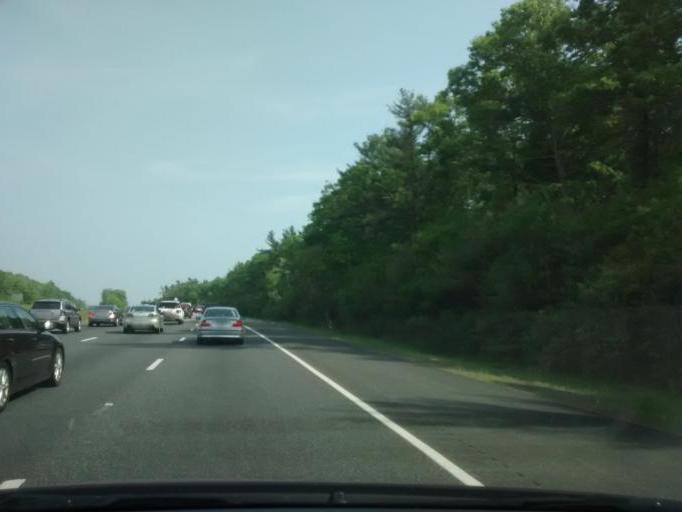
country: US
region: Massachusetts
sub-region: Bristol County
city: Raynham Center
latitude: 41.9390
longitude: -71.0151
